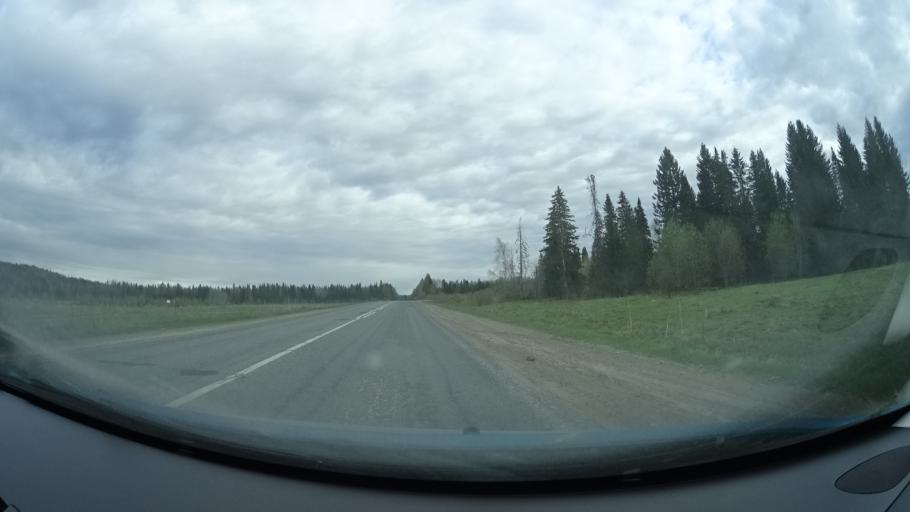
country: RU
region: Perm
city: Yugo-Kamskiy
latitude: 57.6725
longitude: 55.5836
